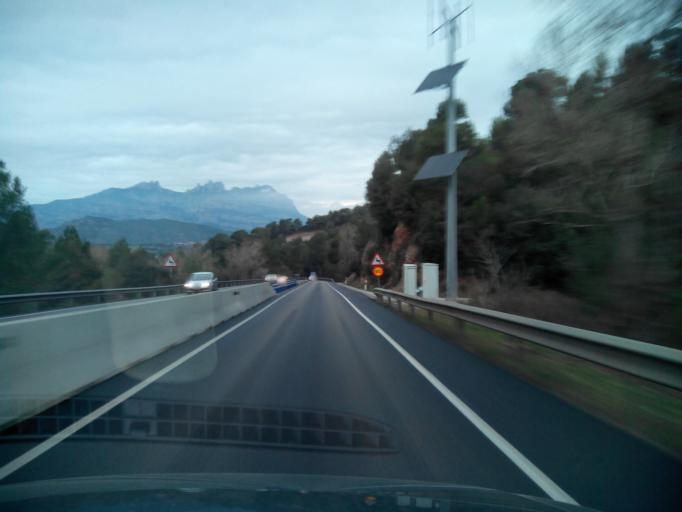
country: ES
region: Catalonia
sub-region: Provincia de Barcelona
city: Viladecavalls
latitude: 41.5842
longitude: 1.9356
